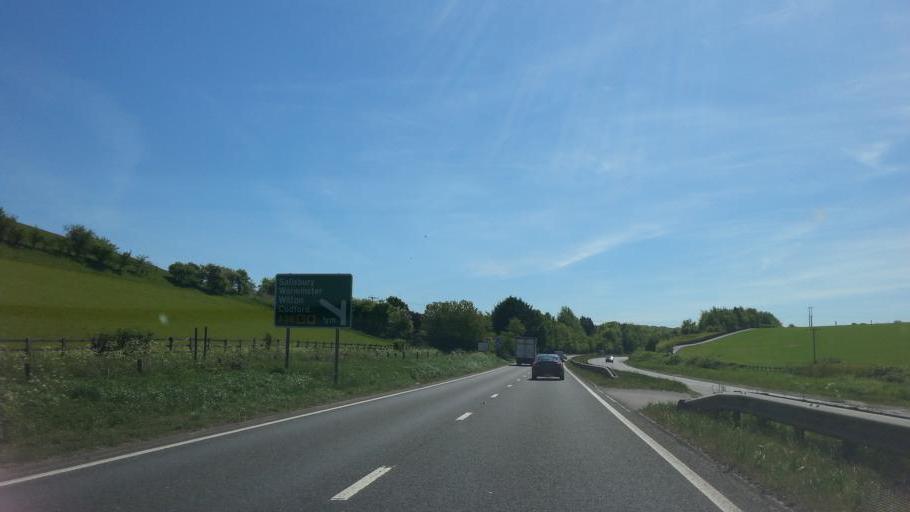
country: GB
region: England
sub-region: Wiltshire
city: Stockton
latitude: 51.1486
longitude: -1.9783
